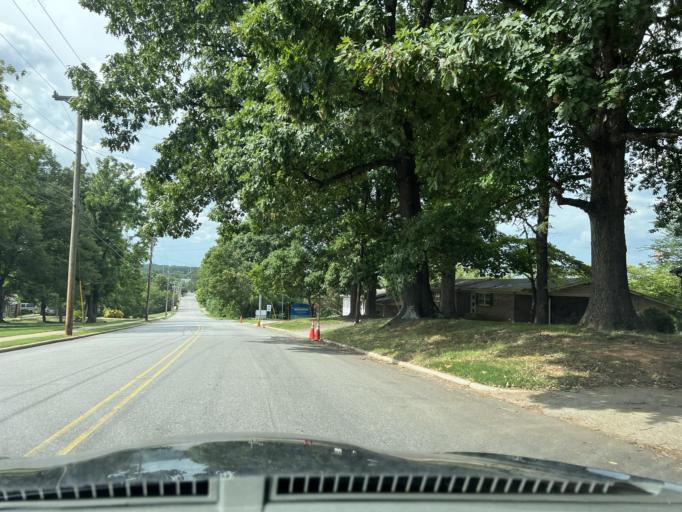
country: US
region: North Carolina
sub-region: Iredell County
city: Statesville
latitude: 35.8019
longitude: -80.8770
